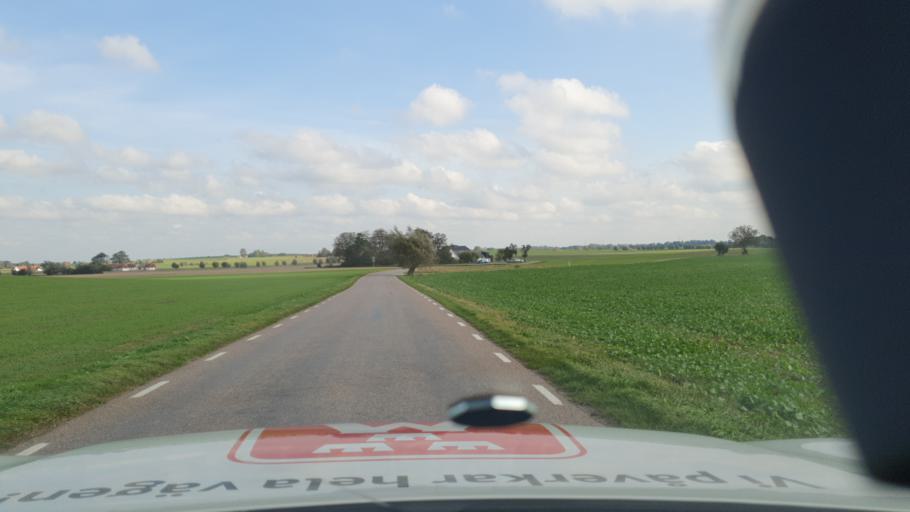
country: SE
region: Skane
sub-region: Vellinge Kommun
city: Vellinge
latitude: 55.4508
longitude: 13.0896
